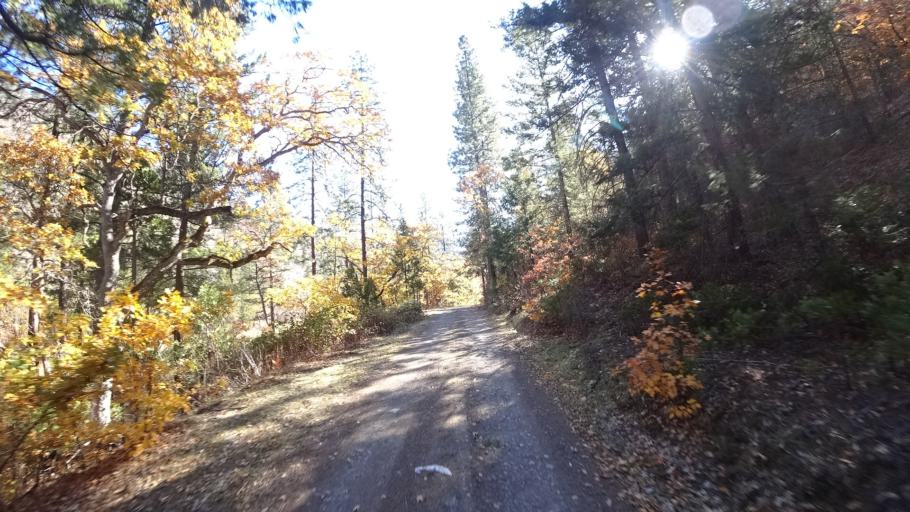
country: US
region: California
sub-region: Siskiyou County
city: Yreka
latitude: 41.8592
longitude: -122.7788
